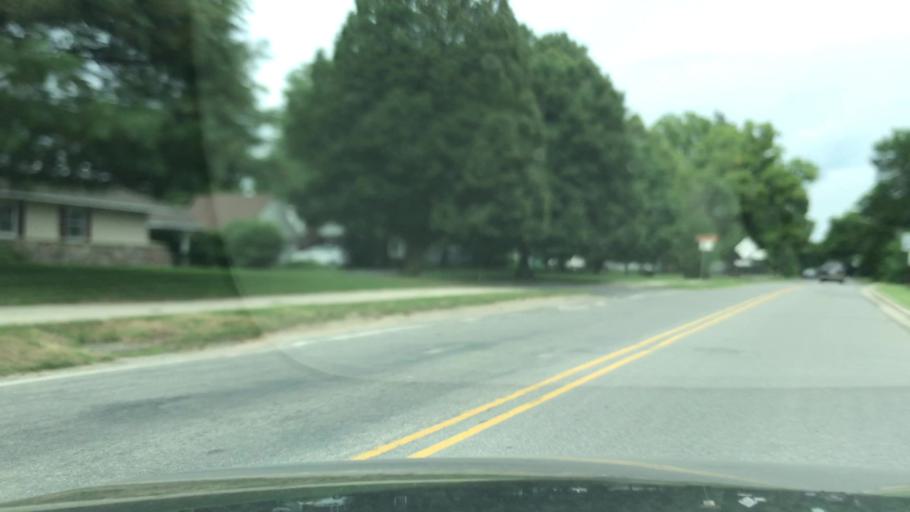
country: US
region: Michigan
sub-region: Kent County
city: East Grand Rapids
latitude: 42.9483
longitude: -85.5556
